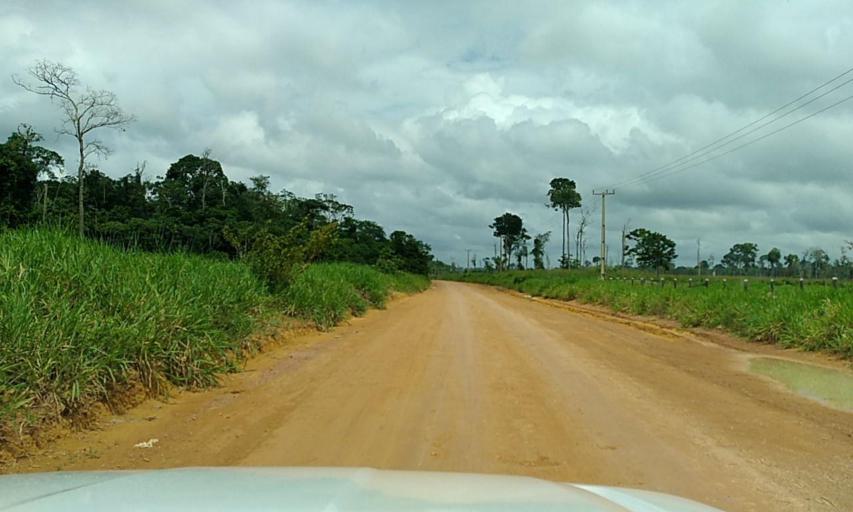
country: BR
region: Para
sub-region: Senador Jose Porfirio
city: Senador Jose Porfirio
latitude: -2.7846
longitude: -51.7703
